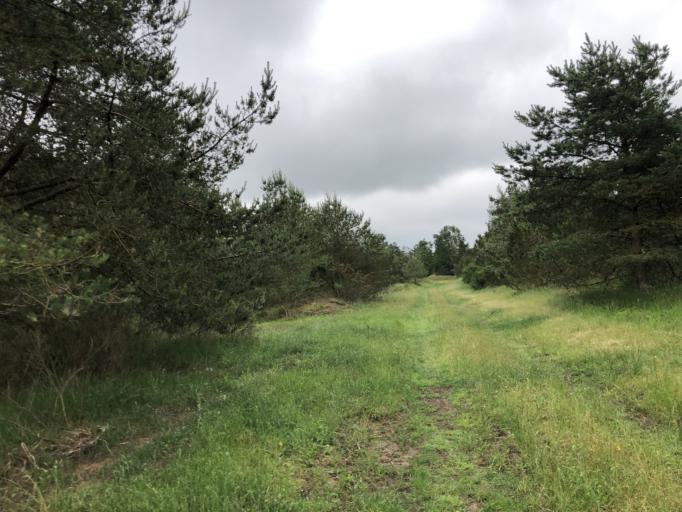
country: DK
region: Central Jutland
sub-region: Holstebro Kommune
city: Ulfborg
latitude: 56.2493
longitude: 8.3626
